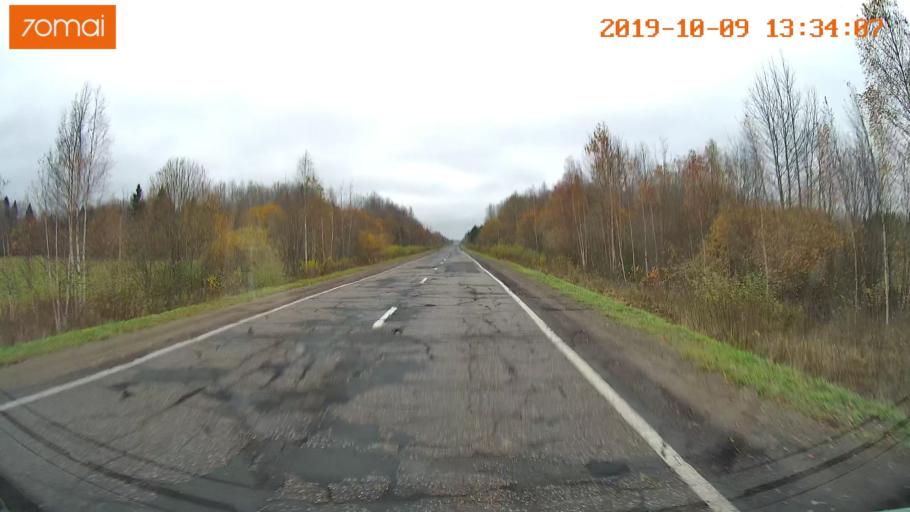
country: RU
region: Jaroslavl
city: Lyubim
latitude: 58.3288
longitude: 41.0569
